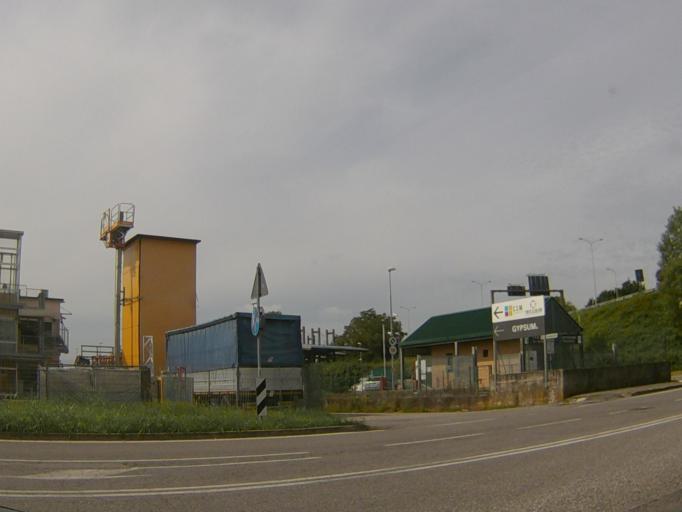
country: IT
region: Lombardy
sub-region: Provincia di Bergamo
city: Treviolo
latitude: 45.6812
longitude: 9.6188
